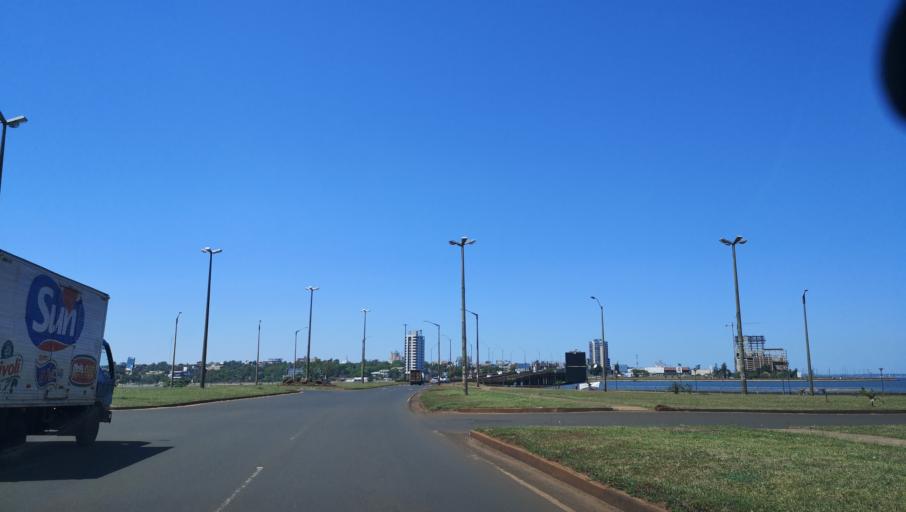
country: PY
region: Itapua
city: Encarnacion
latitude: -27.3149
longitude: -55.8760
